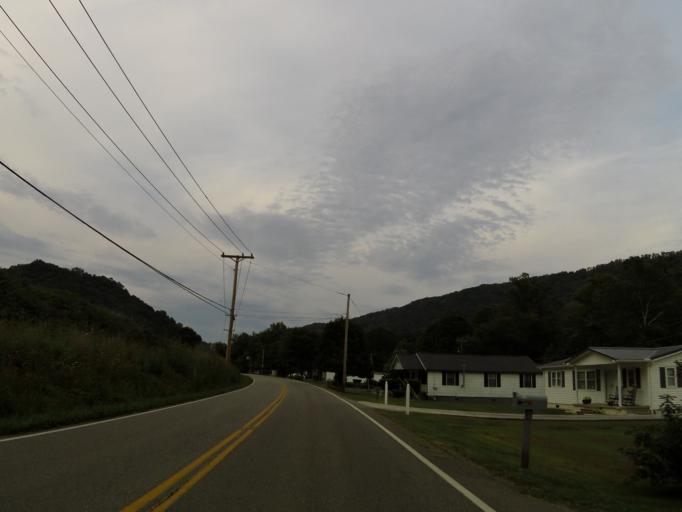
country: US
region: Tennessee
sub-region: Anderson County
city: Rocky Top
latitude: 36.1977
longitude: -84.1710
